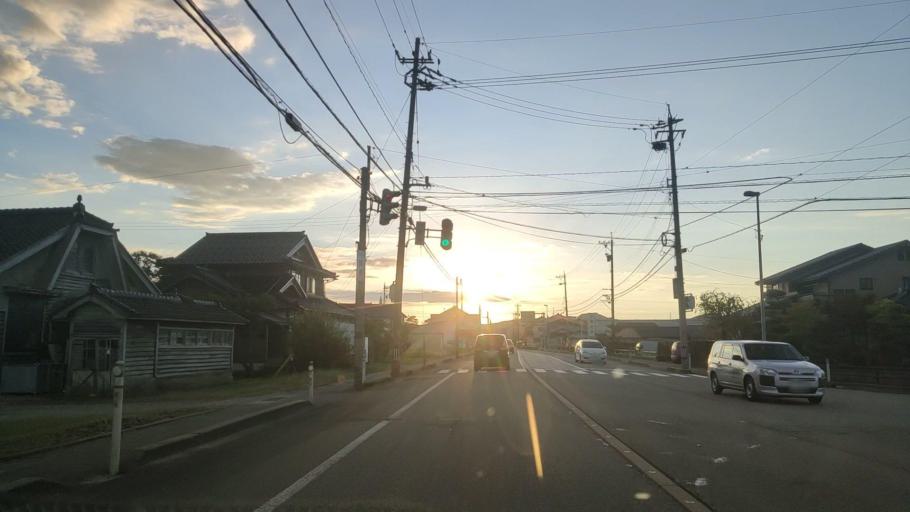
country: JP
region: Toyama
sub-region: Oyabe Shi
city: Oyabe
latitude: 36.6320
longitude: 136.8566
